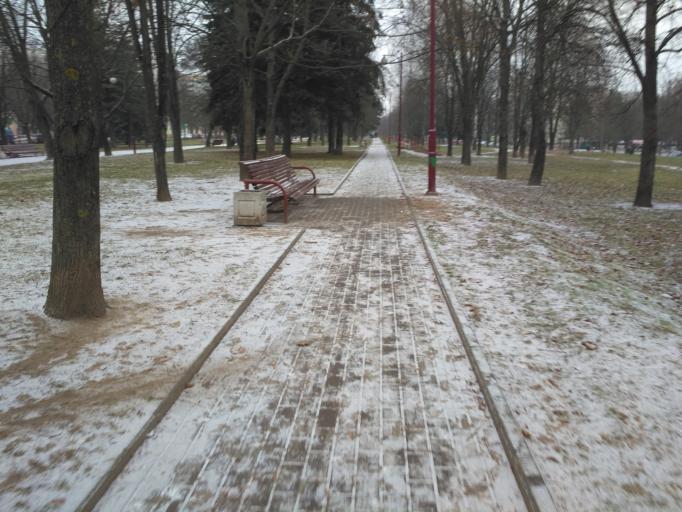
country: BY
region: Minsk
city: Novoye Medvezhino
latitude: 53.9106
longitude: 27.4882
